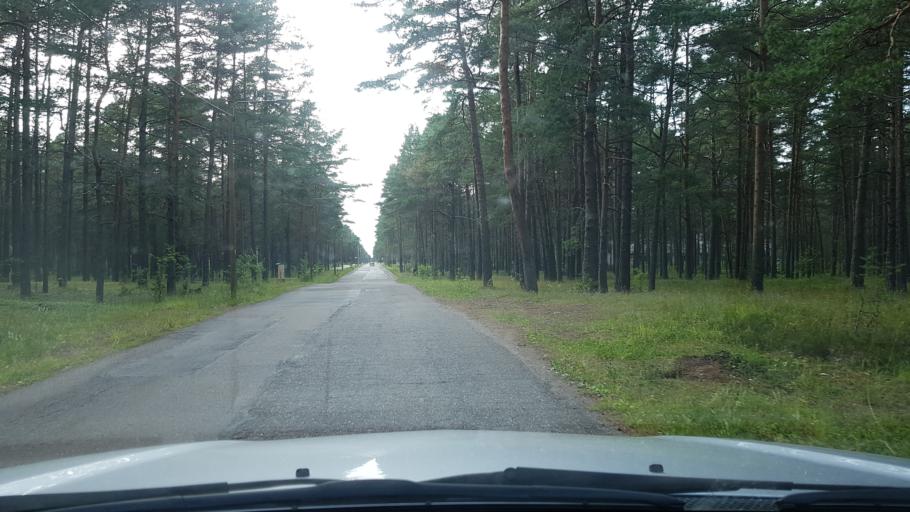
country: EE
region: Ida-Virumaa
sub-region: Narva-Joesuu linn
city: Narva-Joesuu
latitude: 59.4505
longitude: 28.0622
